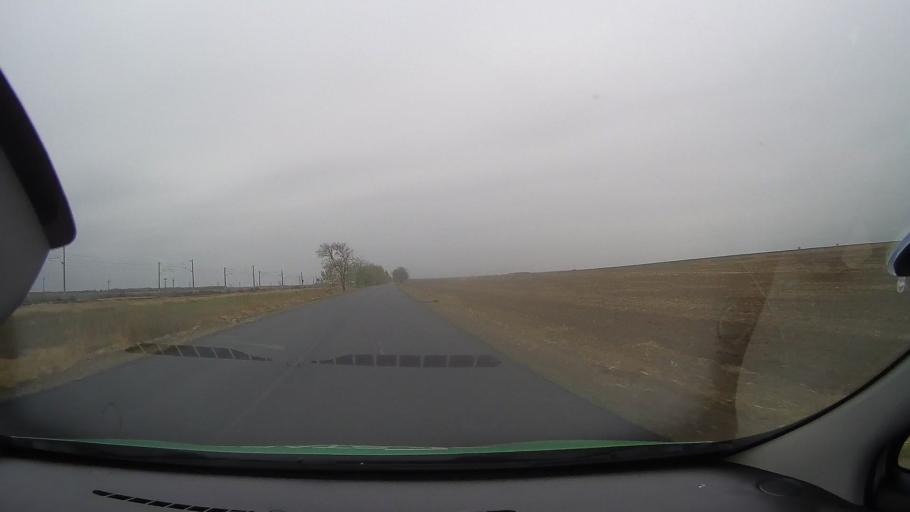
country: RO
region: Ialomita
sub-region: Comuna Valea Ciorii
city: Valea Ciorii
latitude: 44.7010
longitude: 27.5974
